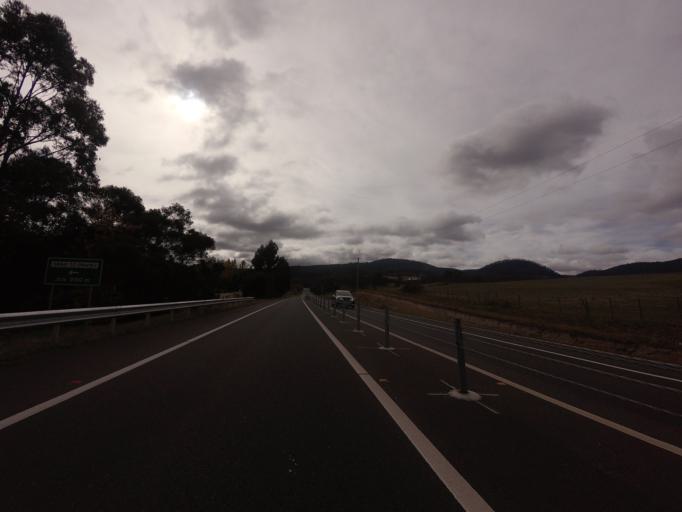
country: AU
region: Tasmania
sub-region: Brighton
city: Bridgewater
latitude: -42.5950
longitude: 147.2215
